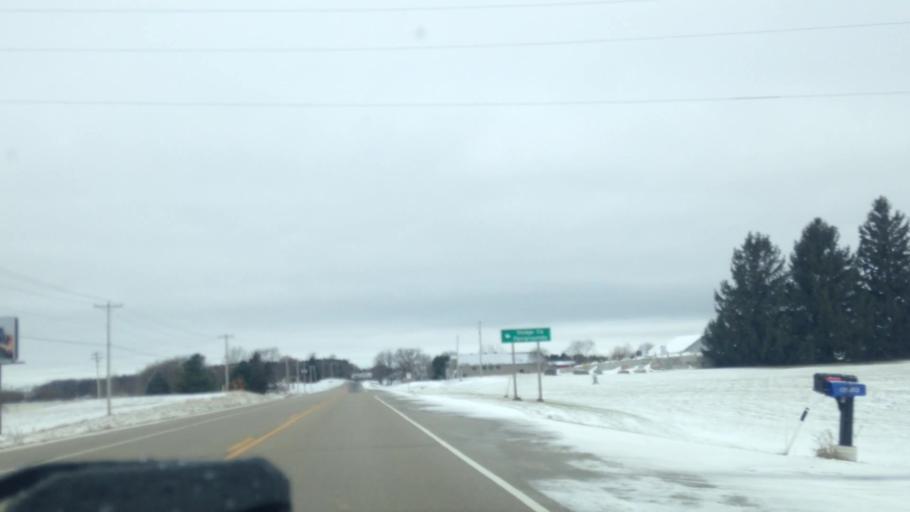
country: US
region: Wisconsin
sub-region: Dodge County
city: Beaver Dam
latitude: 43.4444
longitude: -88.7668
